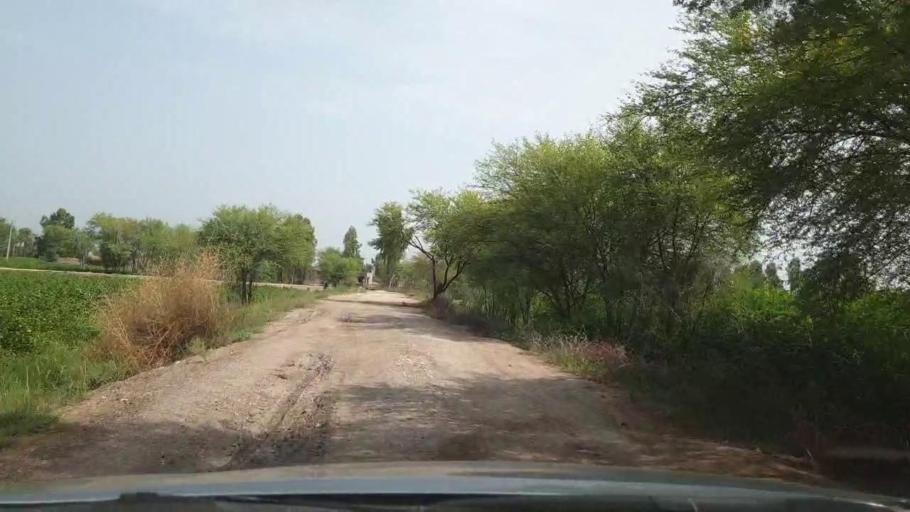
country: PK
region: Sindh
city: Rohri
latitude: 27.6567
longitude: 69.0244
